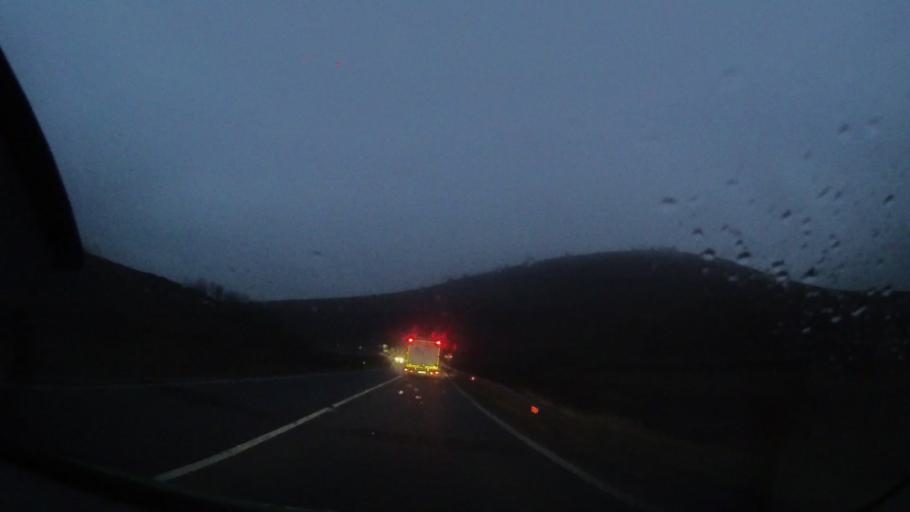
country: RO
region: Harghita
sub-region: Comuna Subcetate
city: Subcetate
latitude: 46.8386
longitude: 25.4841
